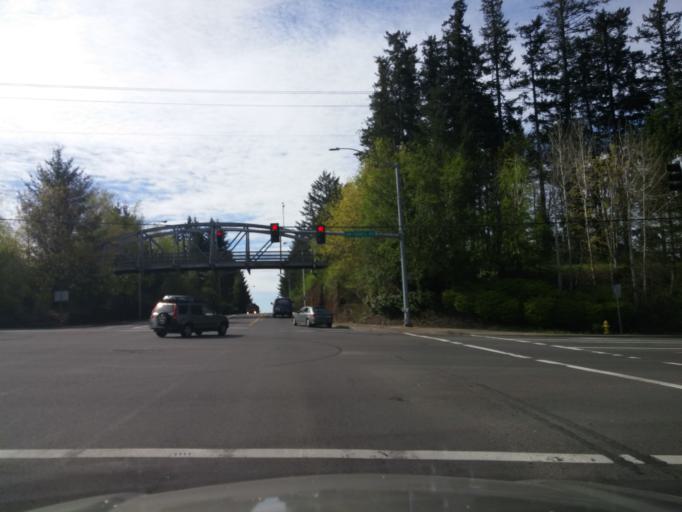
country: US
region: Oregon
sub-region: Washington County
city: Cedar Mill
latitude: 45.5266
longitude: -122.7929
